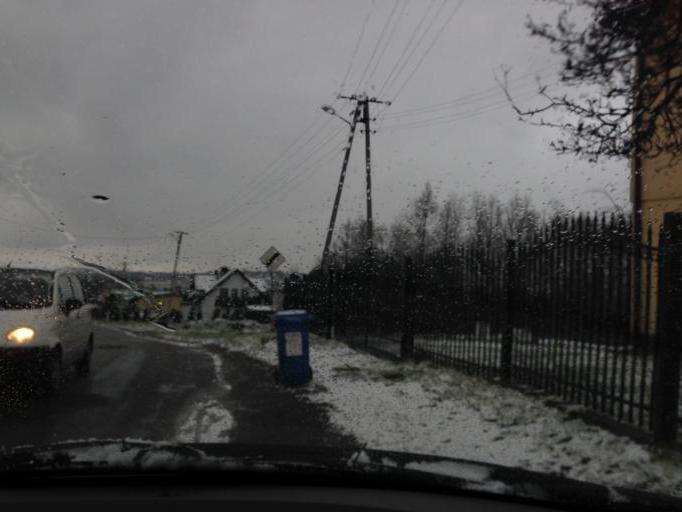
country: PL
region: Lesser Poland Voivodeship
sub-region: Powiat myslenicki
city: Brzaczowice
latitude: 49.8744
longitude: 20.0397
